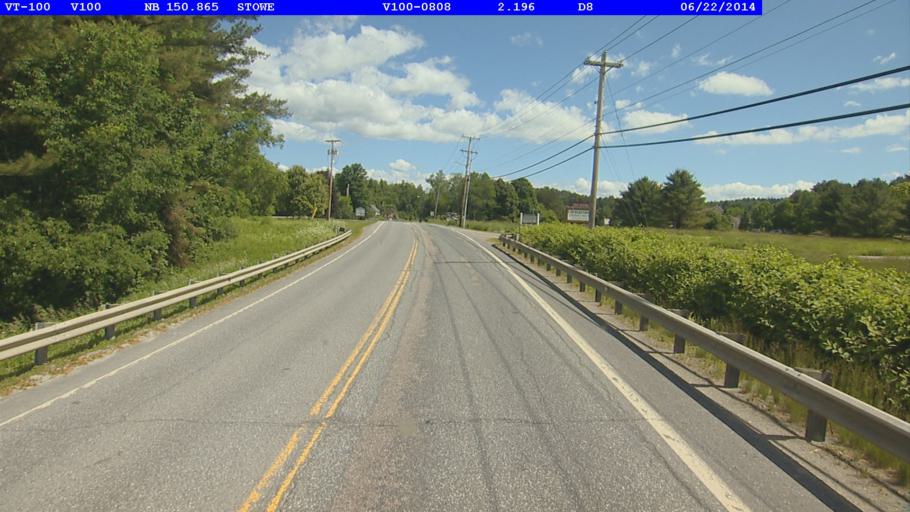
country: US
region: Vermont
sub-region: Washington County
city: Waterbury
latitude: 44.4516
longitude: -72.6974
